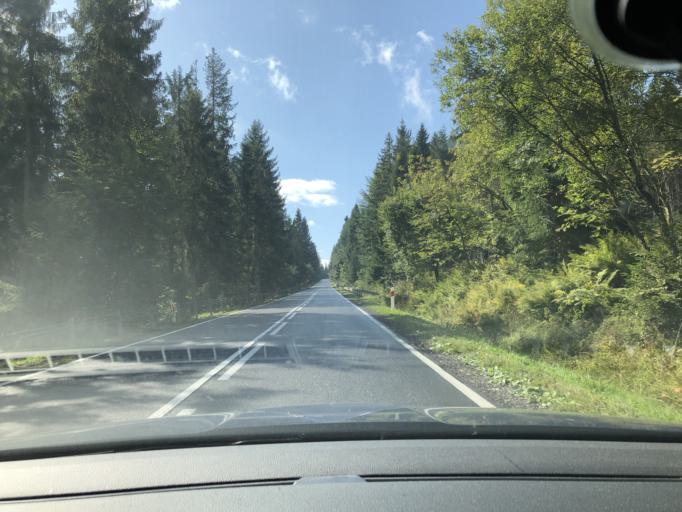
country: PL
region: Lesser Poland Voivodeship
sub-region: Powiat nowotarski
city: Zubrzyca Gorna
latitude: 49.5851
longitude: 19.6058
